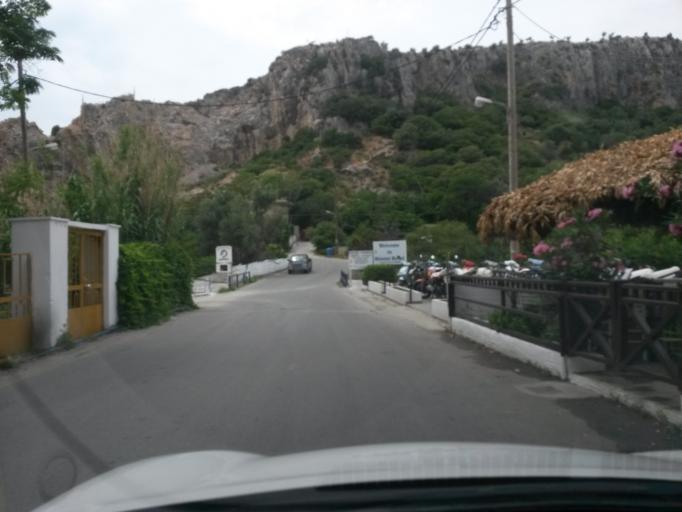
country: GR
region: North Aegean
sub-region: Nomos Lesvou
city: Plomarion
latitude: 38.9695
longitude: 26.3949
